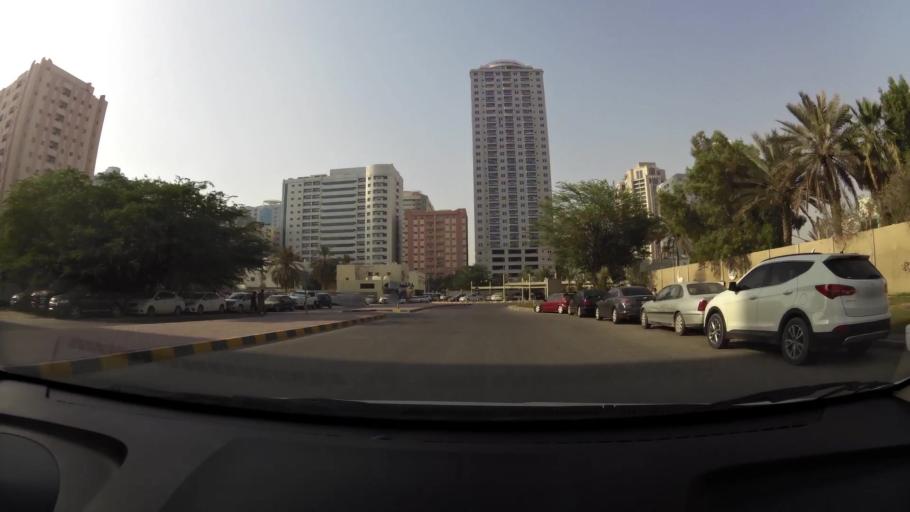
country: AE
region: Ajman
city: Ajman
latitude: 25.3897
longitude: 55.4368
